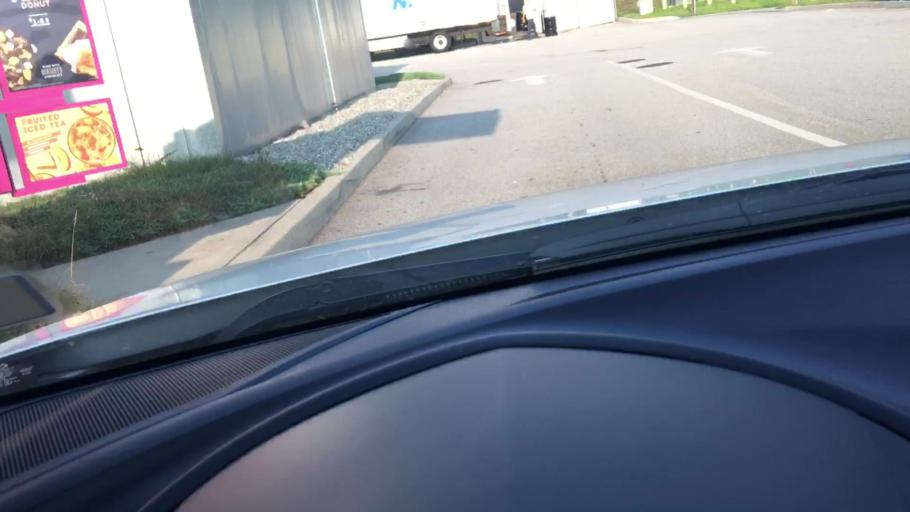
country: US
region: Massachusetts
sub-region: Worcester County
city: Westborough
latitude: 42.2853
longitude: -71.6202
